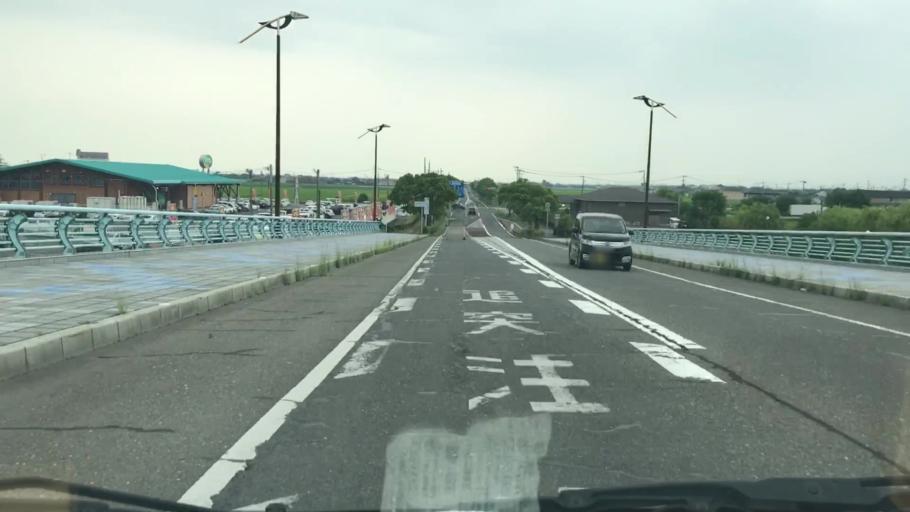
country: JP
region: Saga Prefecture
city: Saga-shi
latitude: 33.2158
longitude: 130.3051
